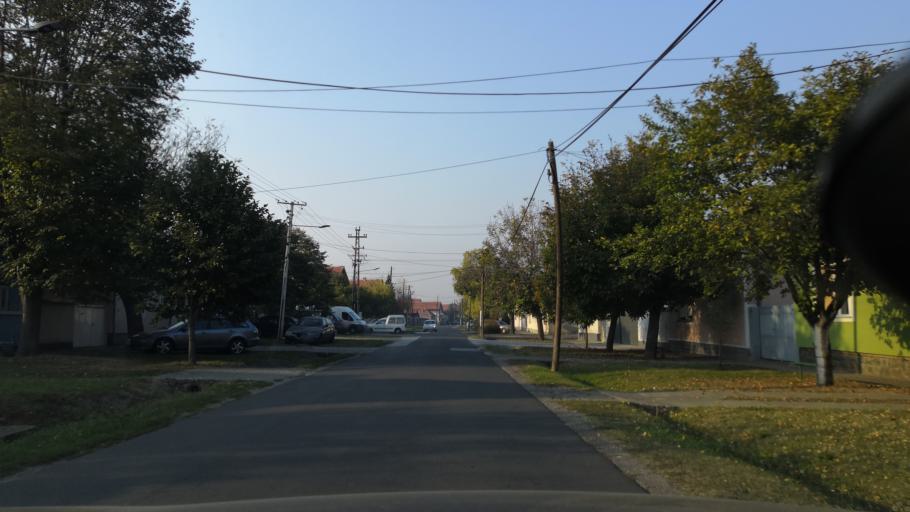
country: RS
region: Autonomna Pokrajina Vojvodina
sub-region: Sremski Okrug
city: Stara Pazova
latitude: 44.9938
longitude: 20.1465
